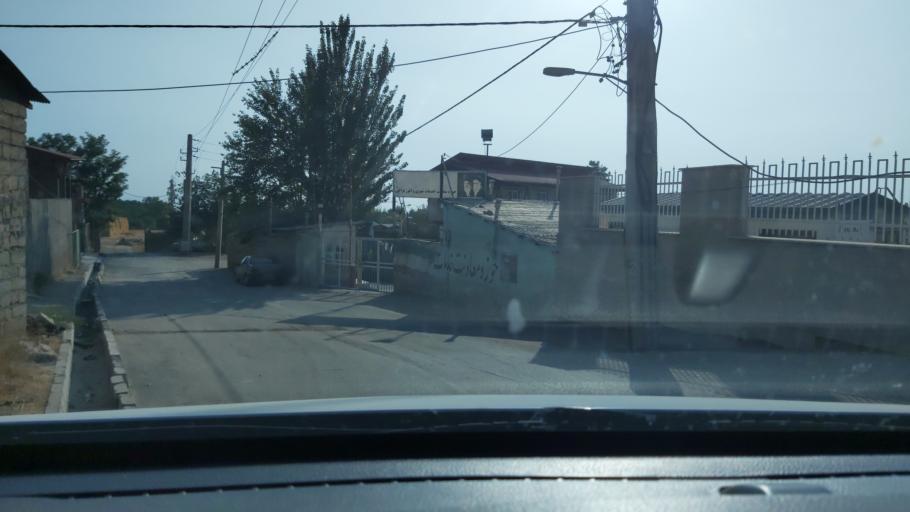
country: IR
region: Alborz
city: Hashtgerd
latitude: 35.9540
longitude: 50.7895
